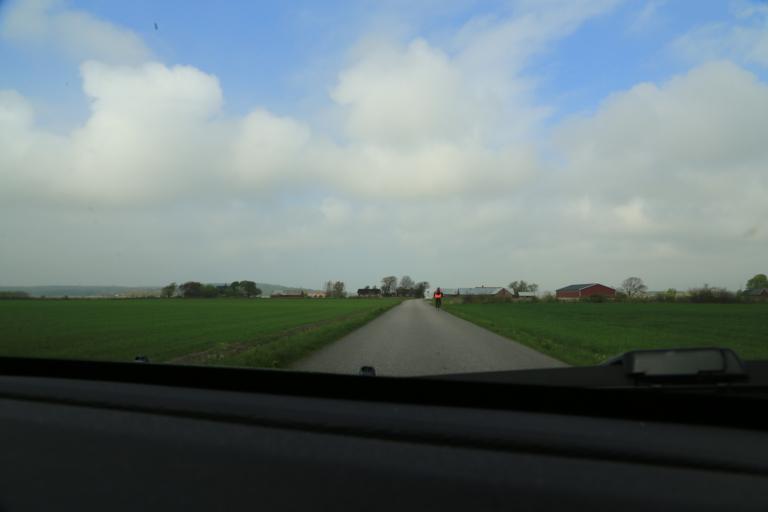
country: SE
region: Halland
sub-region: Kungsbacka Kommun
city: Frillesas
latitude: 57.2293
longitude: 12.1548
